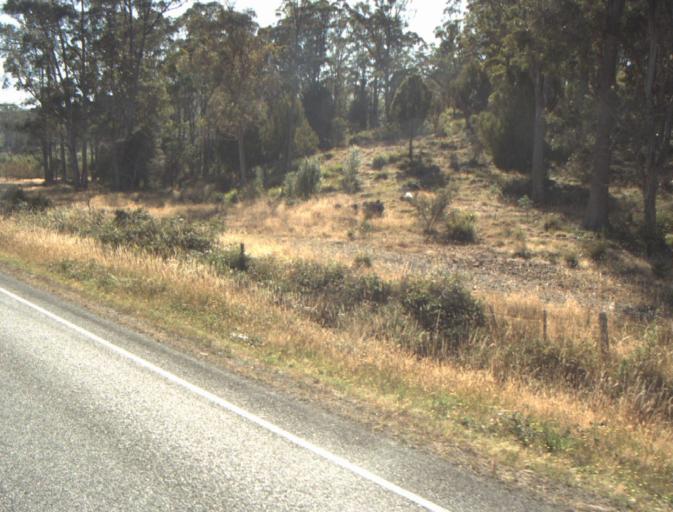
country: AU
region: Tasmania
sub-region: Launceston
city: Newstead
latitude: -41.4025
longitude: 147.2870
